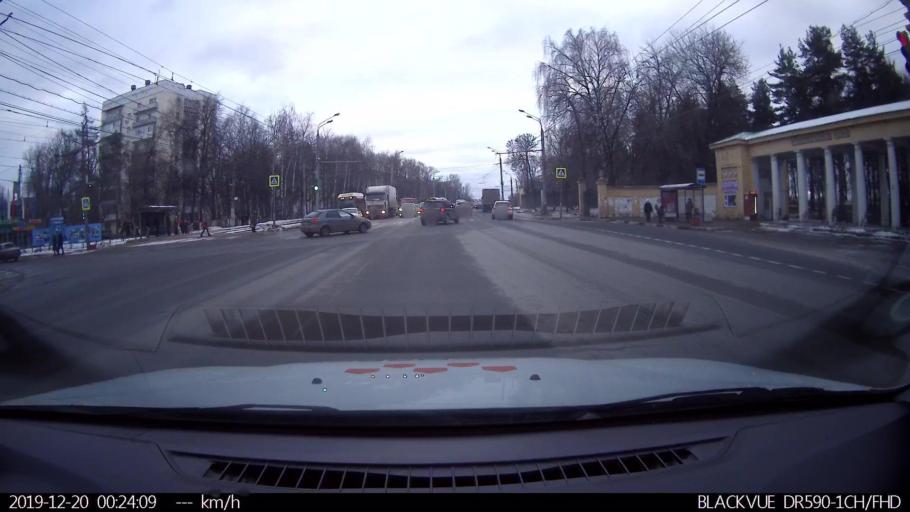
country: RU
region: Vladimir
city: Yur'yev-Pol'skiy
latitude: 56.6876
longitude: 39.5266
